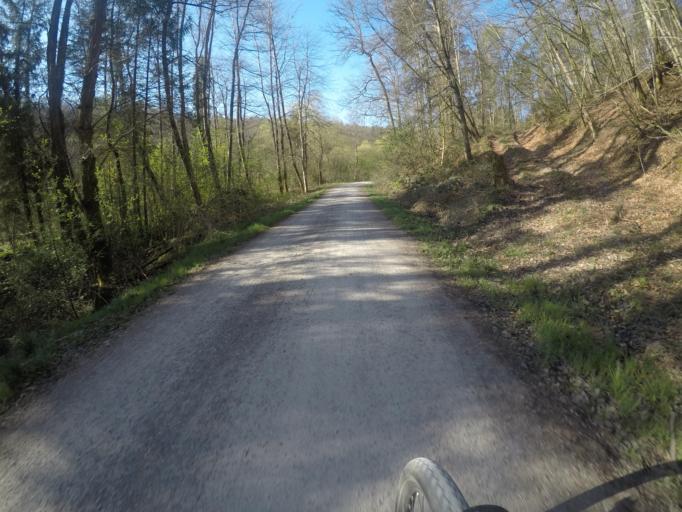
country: DE
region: Baden-Wuerttemberg
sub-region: Regierungsbezirk Stuttgart
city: Schlaitdorf
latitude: 48.6086
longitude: 9.1923
